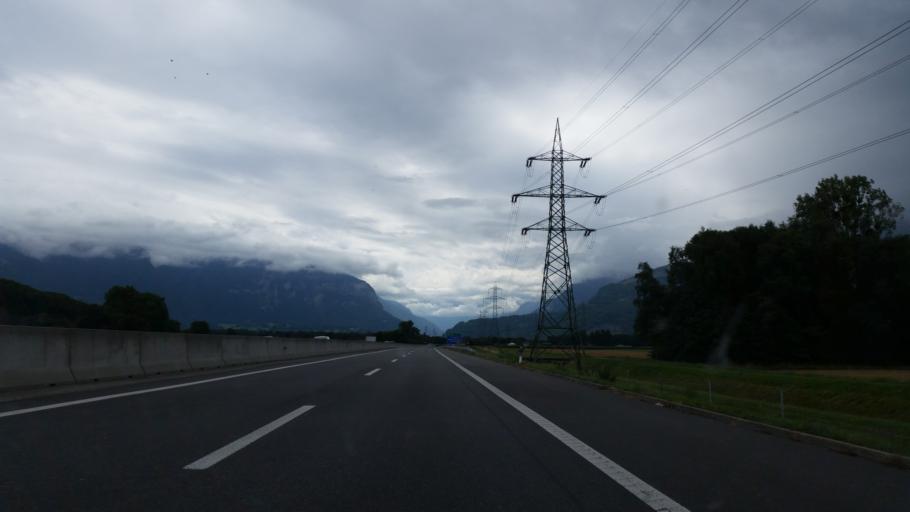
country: CH
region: Valais
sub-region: Monthey District
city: Collombey
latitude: 46.2887
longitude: 6.9632
